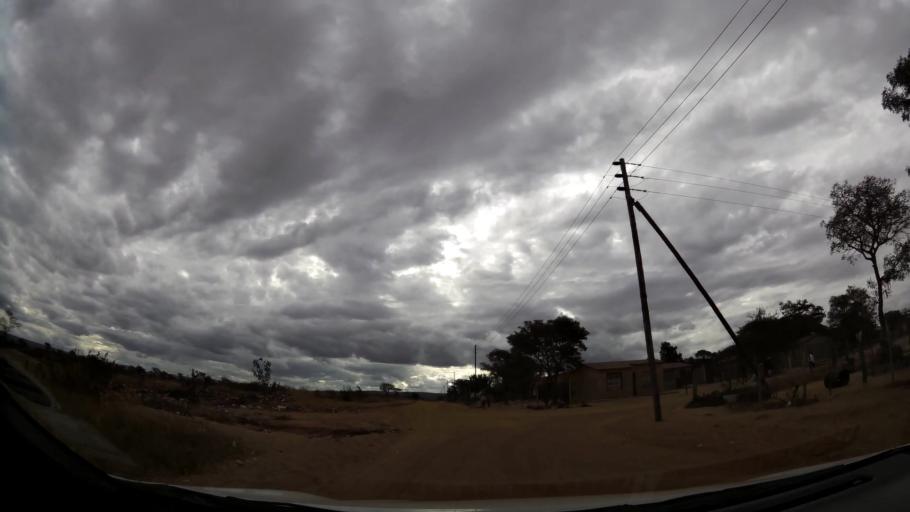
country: ZA
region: Limpopo
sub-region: Waterberg District Municipality
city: Modimolle
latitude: -24.6939
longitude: 28.4230
